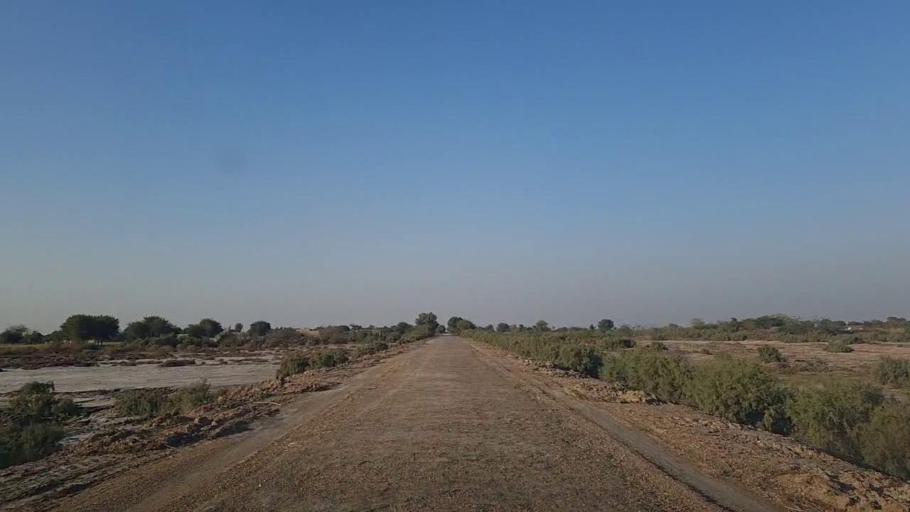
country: PK
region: Sindh
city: Jam Sahib
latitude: 26.2999
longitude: 68.6705
